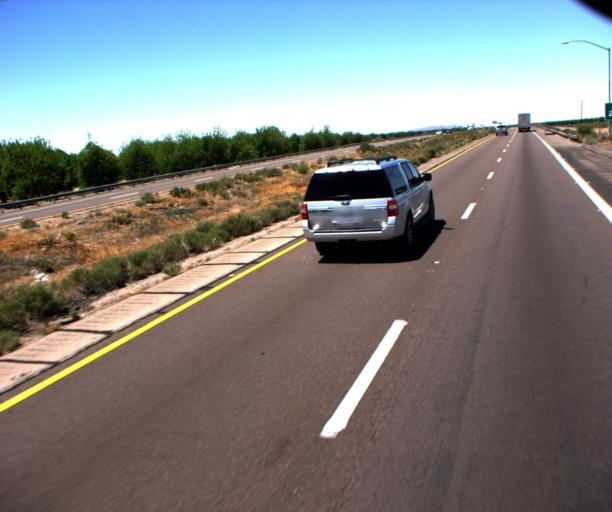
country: US
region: Arizona
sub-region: Pinal County
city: Eloy
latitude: 32.7187
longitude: -111.5082
